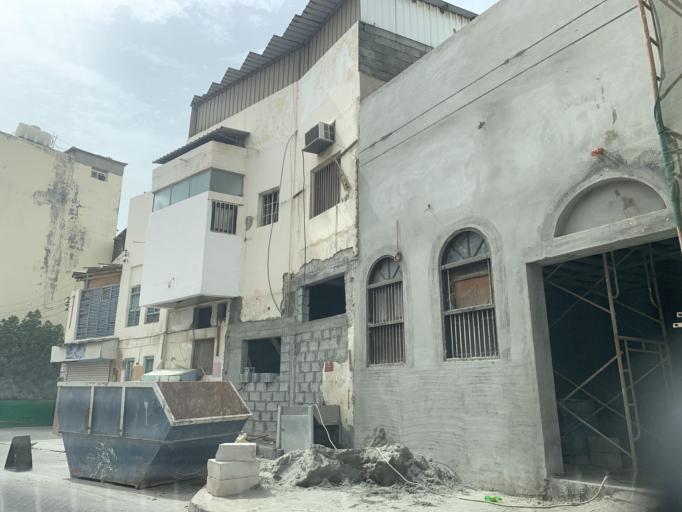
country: BH
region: Manama
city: Manama
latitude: 26.2282
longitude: 50.5787
